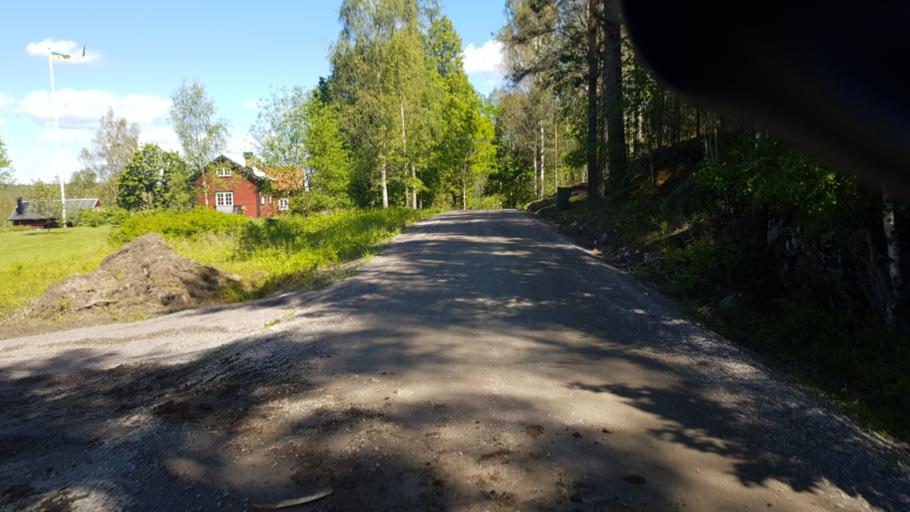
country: SE
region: Vaermland
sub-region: Grums Kommun
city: Grums
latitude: 59.4789
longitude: 12.9289
